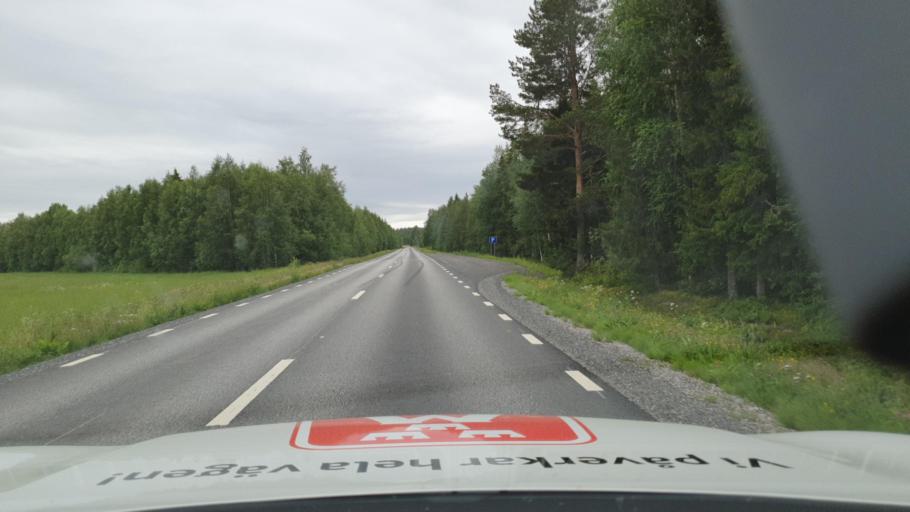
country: SE
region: Vaesterbotten
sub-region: Nordmalings Kommun
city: Nordmaling
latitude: 63.7242
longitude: 19.6471
